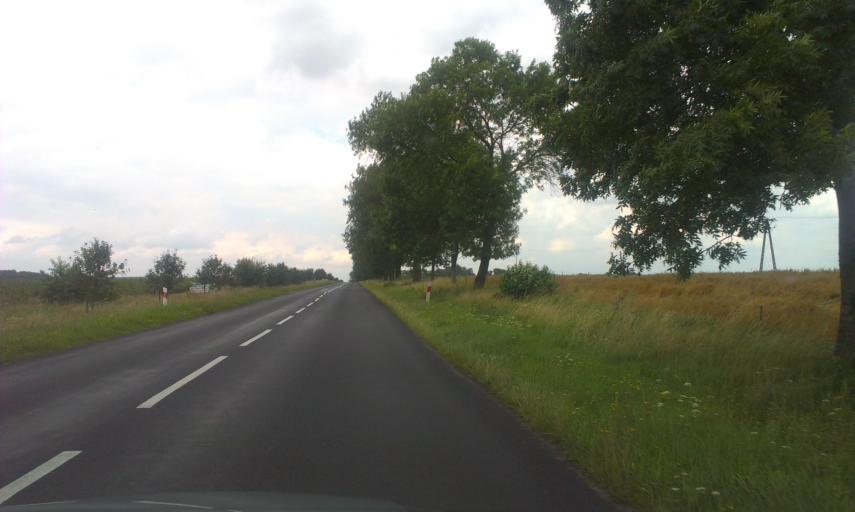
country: PL
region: West Pomeranian Voivodeship
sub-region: Powiat swidwinski
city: Polczyn-Zdroj
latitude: 53.8637
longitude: 16.0703
